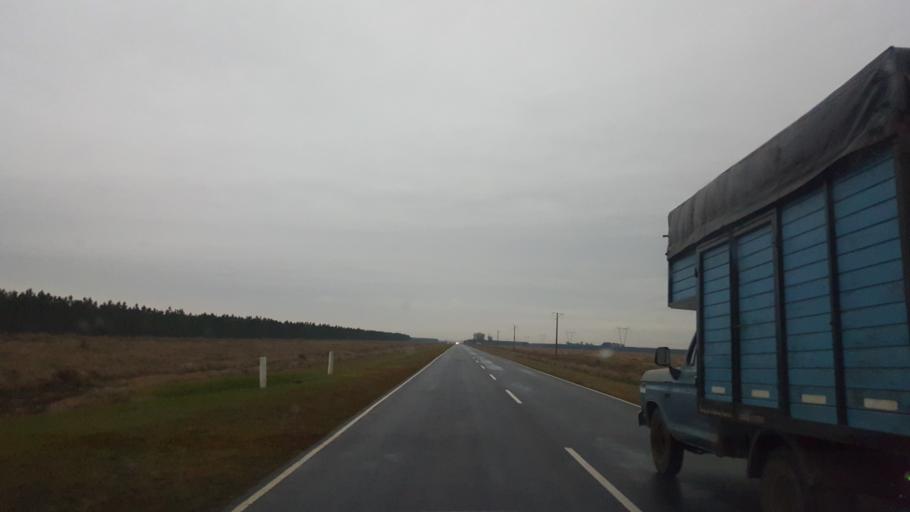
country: PY
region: Itapua
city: San Cosme y Damian
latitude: -27.5722
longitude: -56.2742
